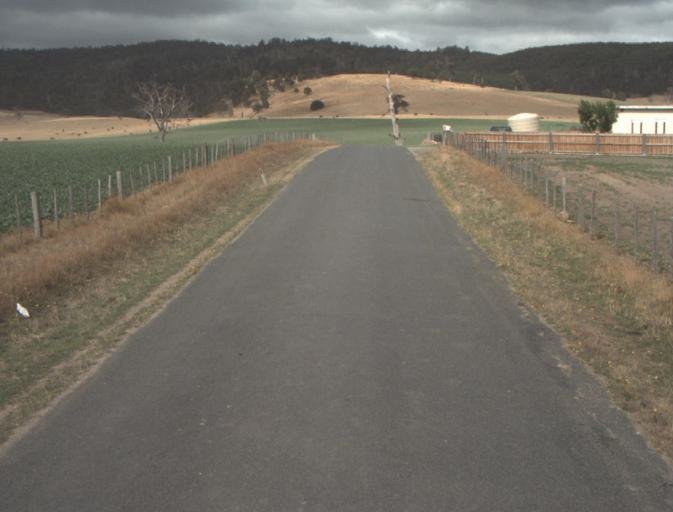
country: AU
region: Tasmania
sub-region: Dorset
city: Scottsdale
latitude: -41.4715
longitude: 147.5887
